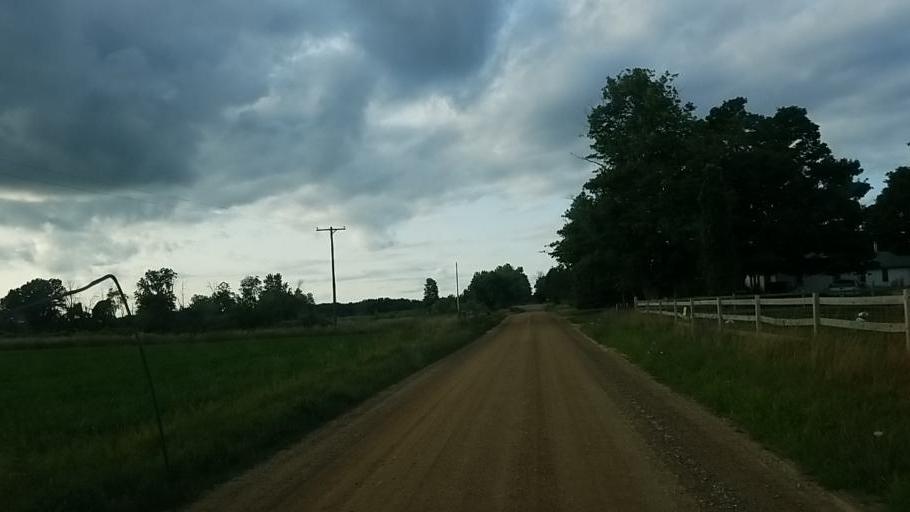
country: US
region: Michigan
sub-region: Montcalm County
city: Howard City
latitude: 43.3352
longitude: -85.3830
